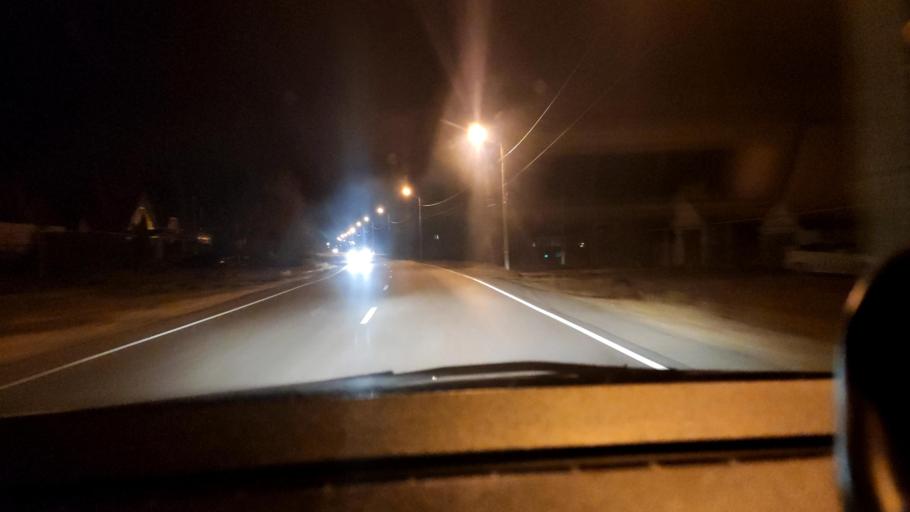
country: RU
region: Voronezj
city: Shilovo
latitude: 51.5717
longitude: 39.0428
